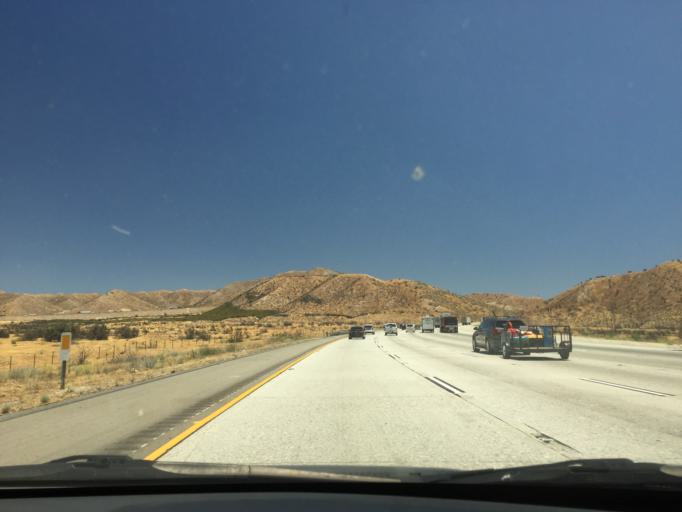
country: US
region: California
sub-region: San Bernardino County
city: Oak Hills
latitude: 34.3393
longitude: -117.4770
